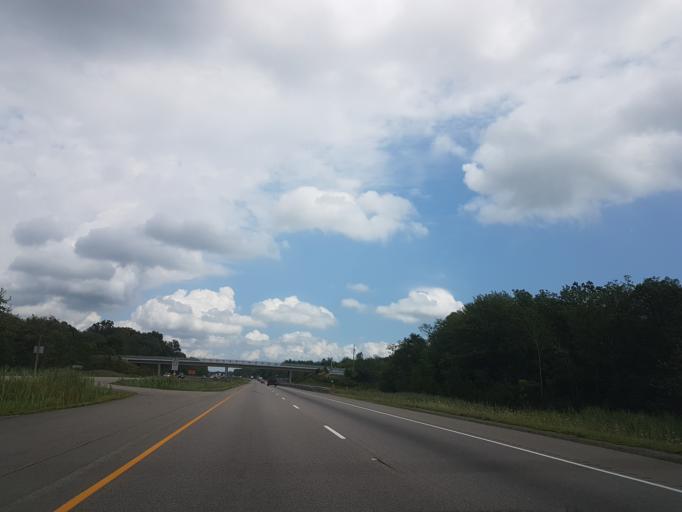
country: CA
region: Ontario
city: Quinte West
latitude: 44.1018
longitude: -77.6868
